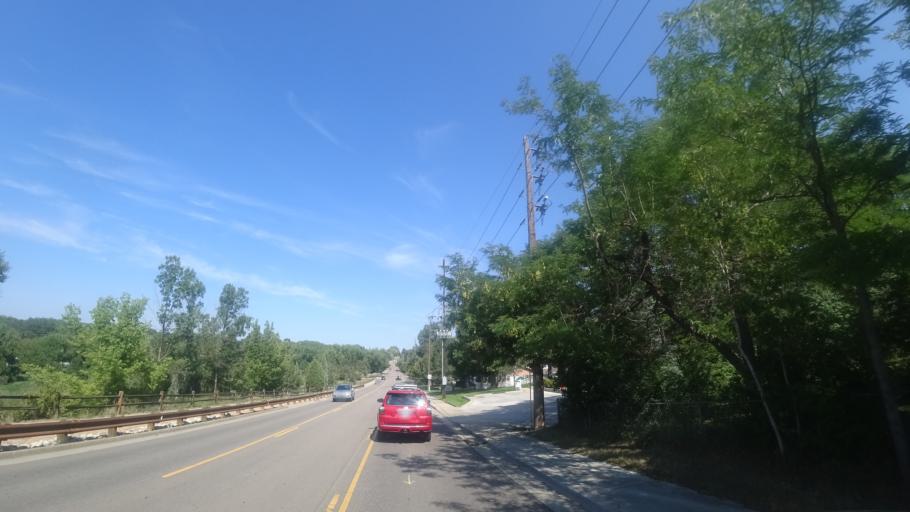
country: US
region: Colorado
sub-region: Arapahoe County
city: Greenwood Village
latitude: 39.6096
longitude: -104.9783
